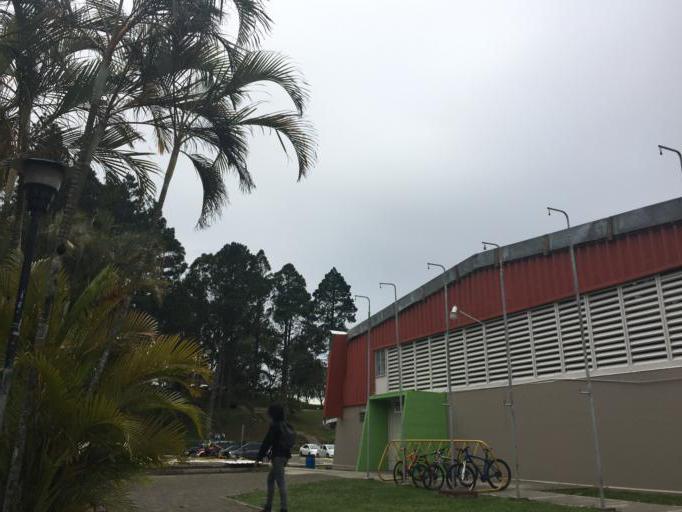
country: CR
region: Cartago
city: Cartago
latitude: 9.8567
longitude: -83.9106
